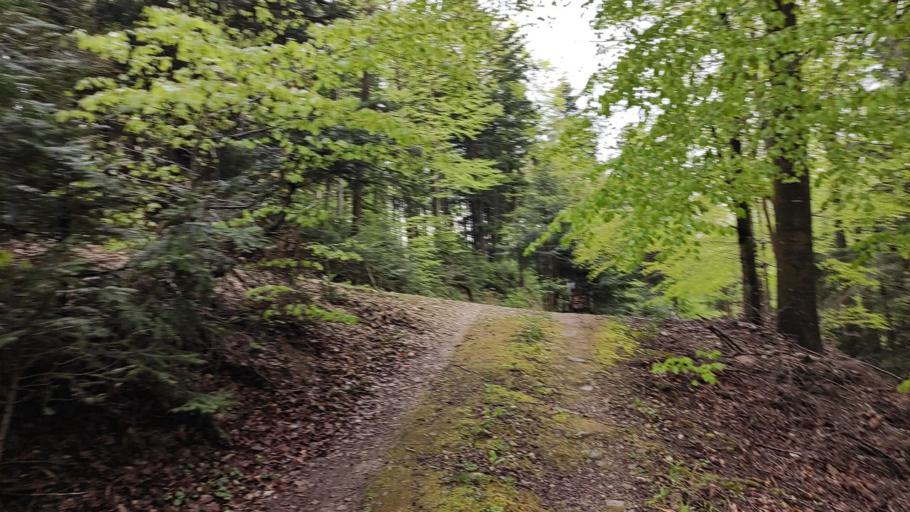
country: DE
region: Baden-Wuerttemberg
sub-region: Freiburg Region
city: Solden
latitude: 47.9133
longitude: 7.8365
